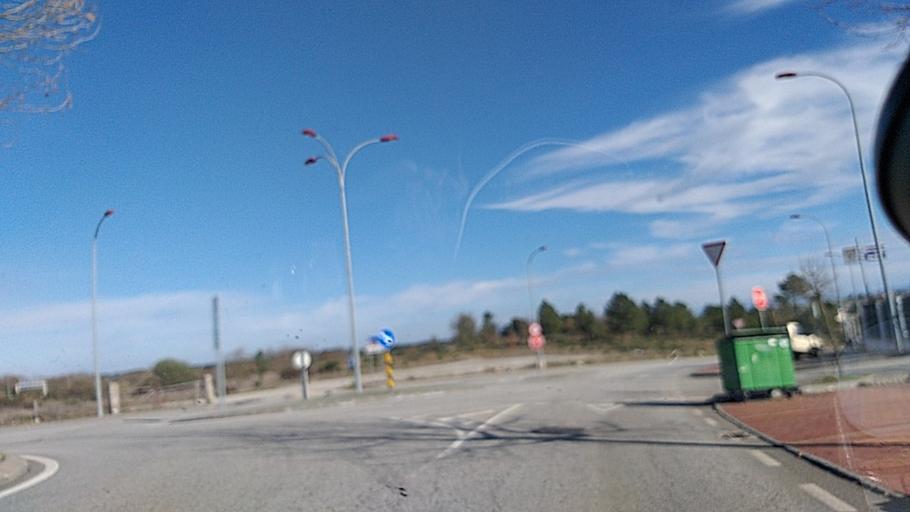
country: ES
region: Castille and Leon
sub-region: Provincia de Salamanca
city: Fuentes de Onoro
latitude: 40.6176
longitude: -6.8423
